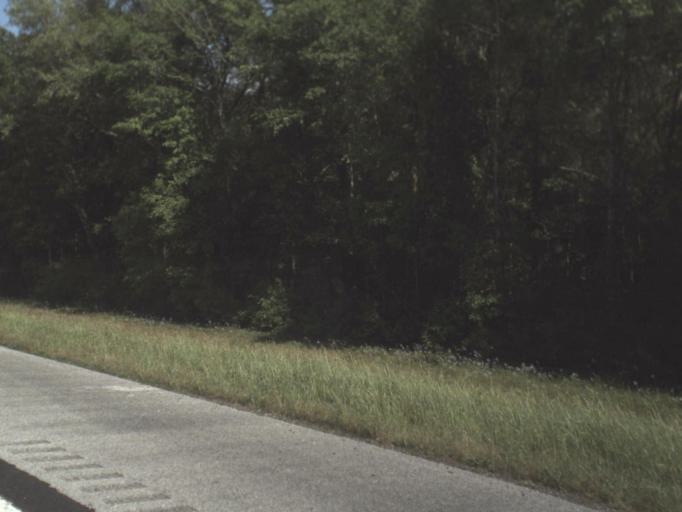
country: US
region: Florida
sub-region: Santa Rosa County
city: East Milton
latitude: 30.6251
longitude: -86.9437
